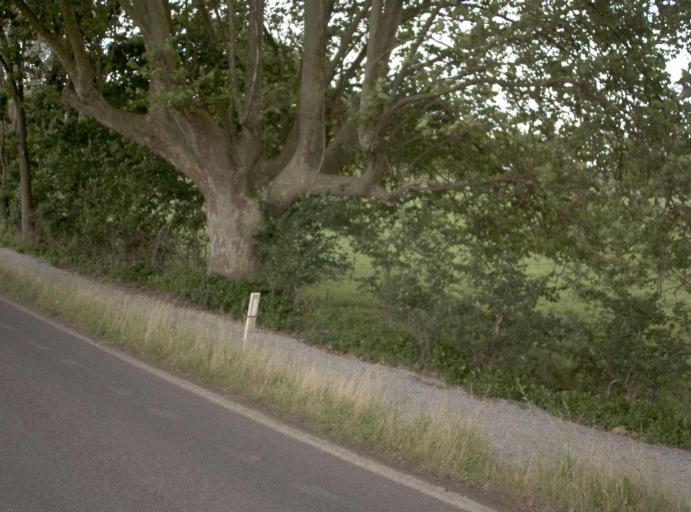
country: AU
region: Victoria
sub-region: Baw Baw
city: Warragul
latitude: -38.1669
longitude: 145.9725
